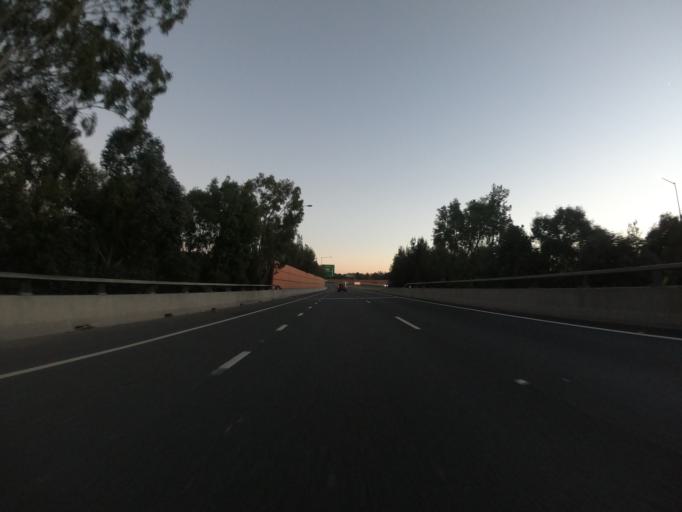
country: AU
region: New South Wales
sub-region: Liverpool
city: Miller
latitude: -33.9300
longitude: 150.8665
